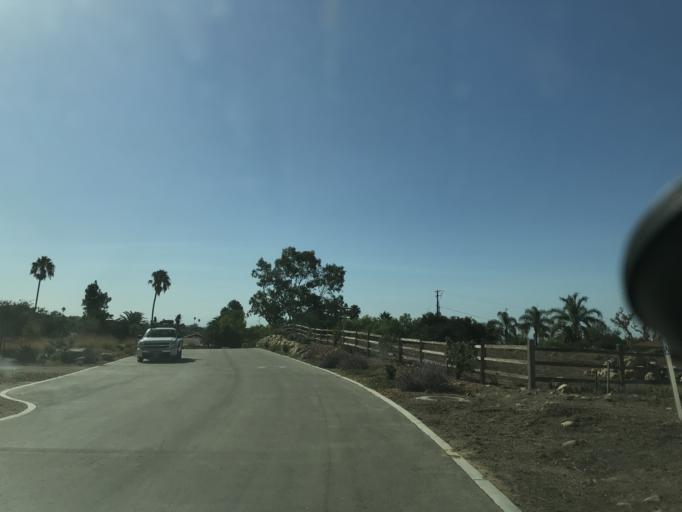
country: US
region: California
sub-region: Santa Barbara County
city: Goleta
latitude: 34.4574
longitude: -119.7865
